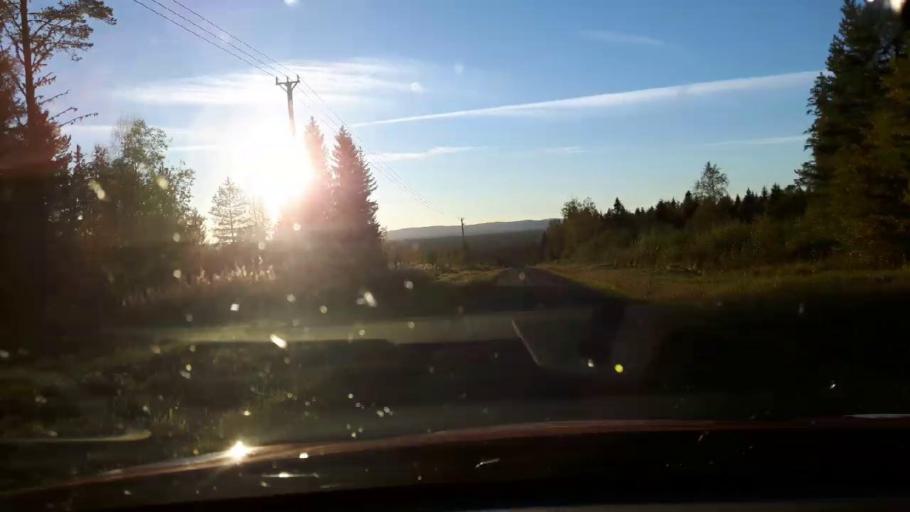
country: SE
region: Jaemtland
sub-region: Krokoms Kommun
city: Krokom
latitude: 63.4519
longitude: 14.5493
